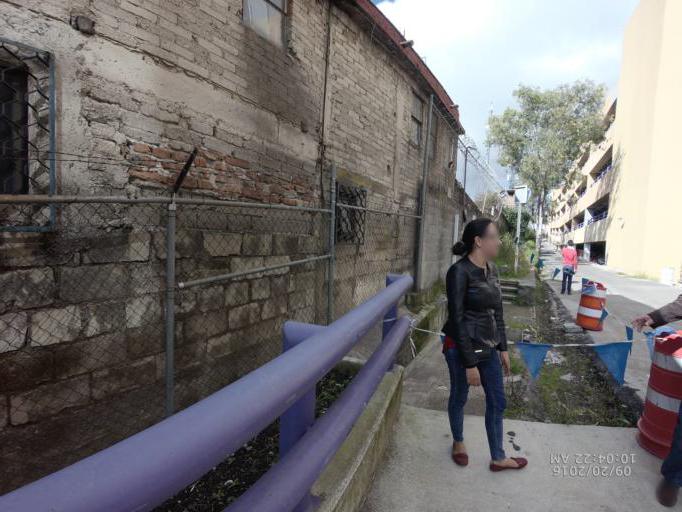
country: MX
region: Mexico City
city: Col. Bosques de las Lomas
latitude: 19.3574
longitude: -99.2586
